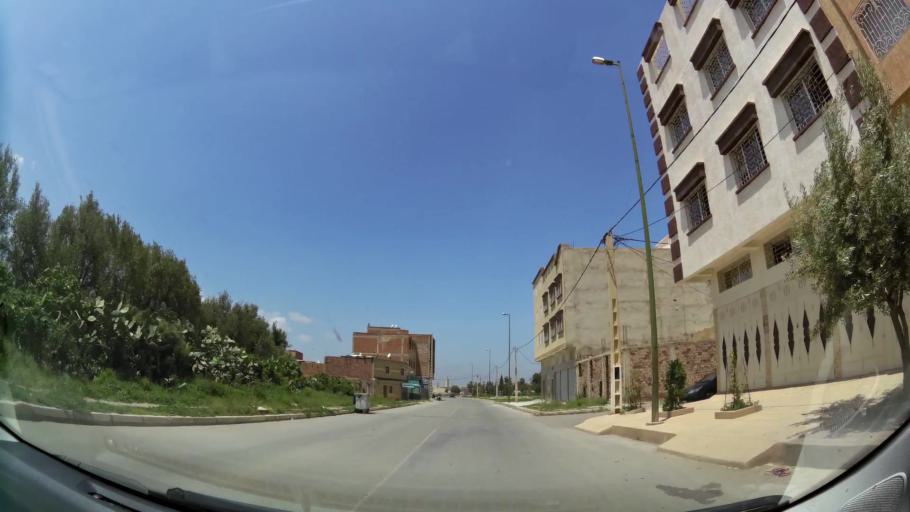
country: MA
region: Oriental
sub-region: Oujda-Angad
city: Oujda
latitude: 34.6885
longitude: -1.8965
